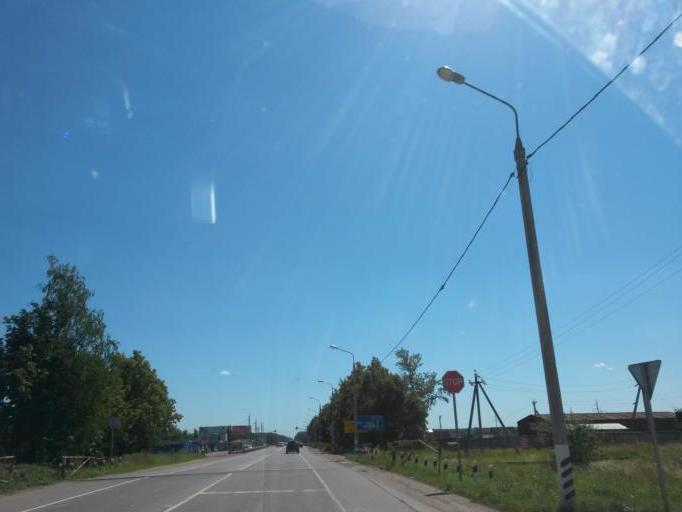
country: RU
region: Moskovskaya
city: Proletarskiy
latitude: 55.0297
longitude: 37.4278
